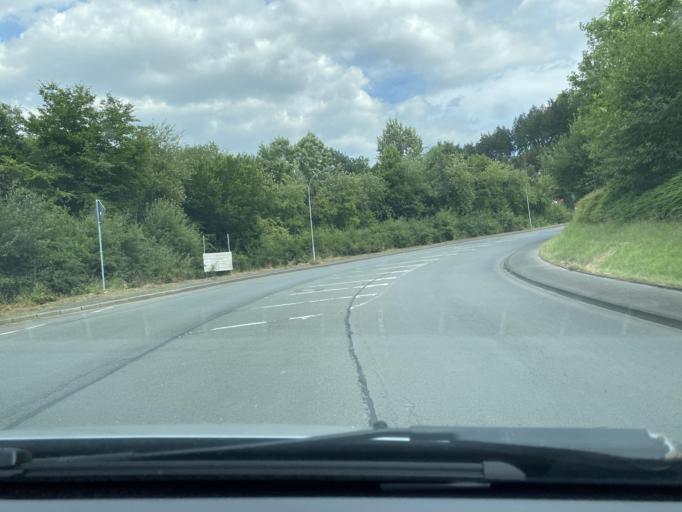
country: DE
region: North Rhine-Westphalia
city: Werdohl
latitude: 51.2604
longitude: 7.7804
